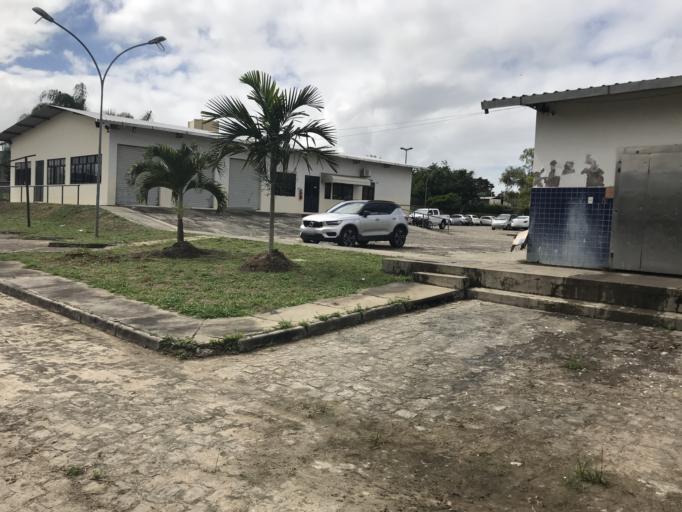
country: BR
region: Bahia
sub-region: Santo Antonio De Jesus
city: Santo Antonio de Jesus
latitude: -12.9798
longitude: -39.2824
